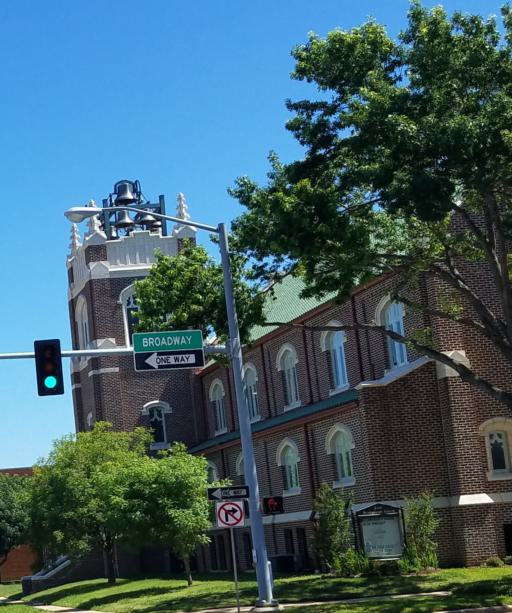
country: US
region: Oklahoma
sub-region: Carter County
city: Ardmore
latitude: 34.1740
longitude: -97.1324
